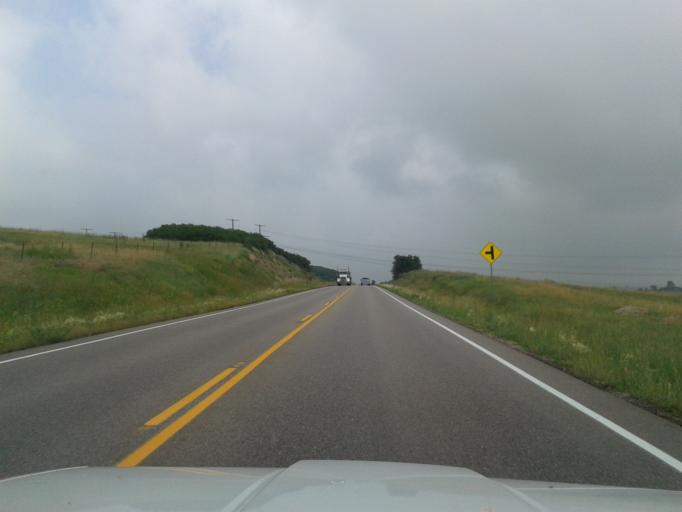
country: US
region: Colorado
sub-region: Douglas County
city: Castle Rock
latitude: 39.2834
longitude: -104.7366
